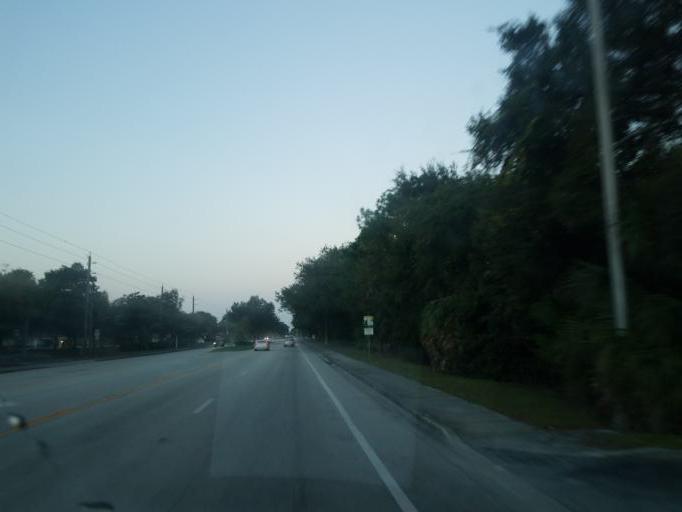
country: US
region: Florida
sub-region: Sarasota County
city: The Meadows
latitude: 27.3521
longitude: -82.4651
